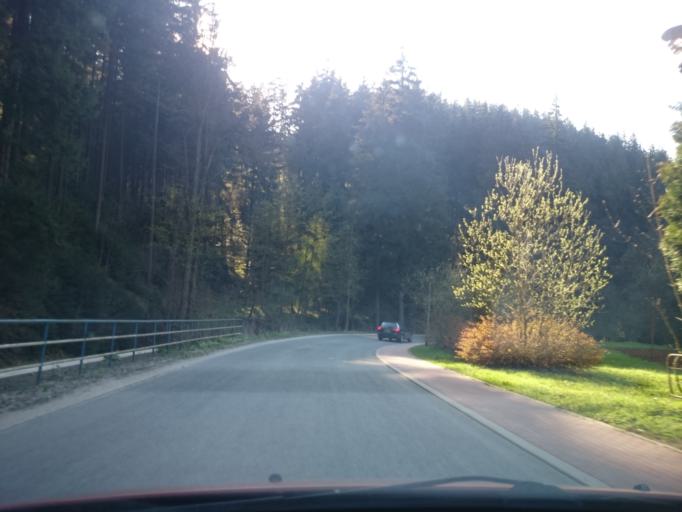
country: PL
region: Lower Silesian Voivodeship
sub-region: Powiat klodzki
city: Duszniki-Zdroj
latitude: 50.3799
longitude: 16.3917
